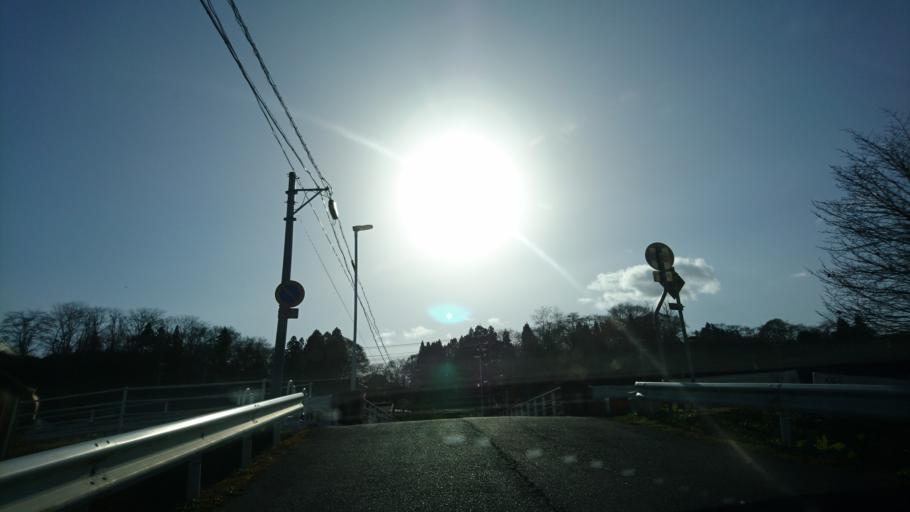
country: JP
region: Iwate
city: Ichinoseki
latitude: 38.9175
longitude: 141.3347
